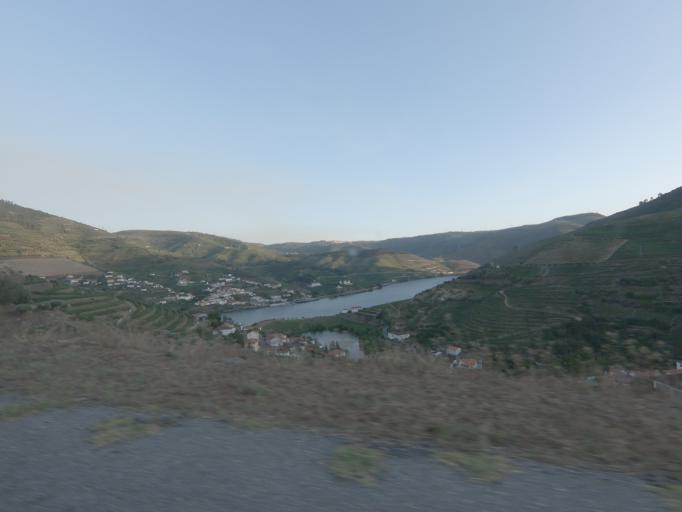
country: PT
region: Viseu
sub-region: Armamar
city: Armamar
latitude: 41.1606
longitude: -7.6824
